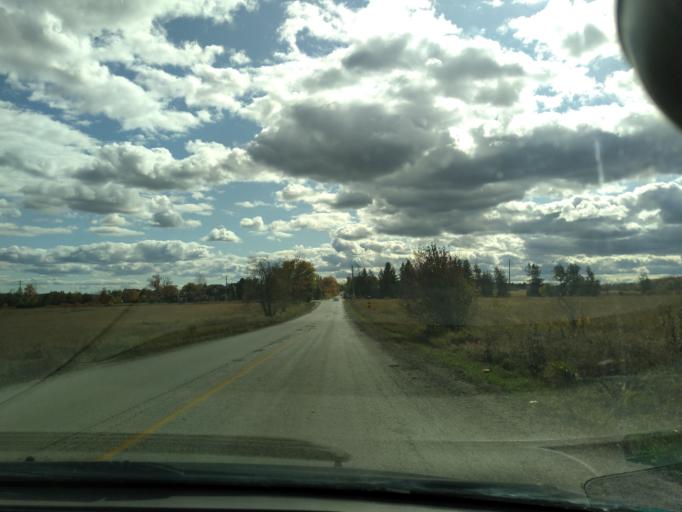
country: CA
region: Ontario
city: Bradford West Gwillimbury
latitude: 44.0836
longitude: -79.5962
